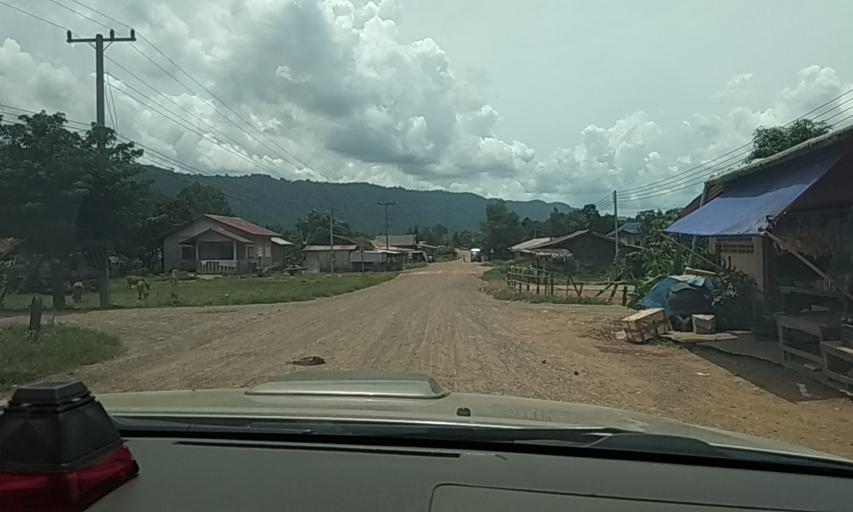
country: LA
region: Bolikhamxai
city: Ban Nahin
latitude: 18.1401
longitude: 104.7610
